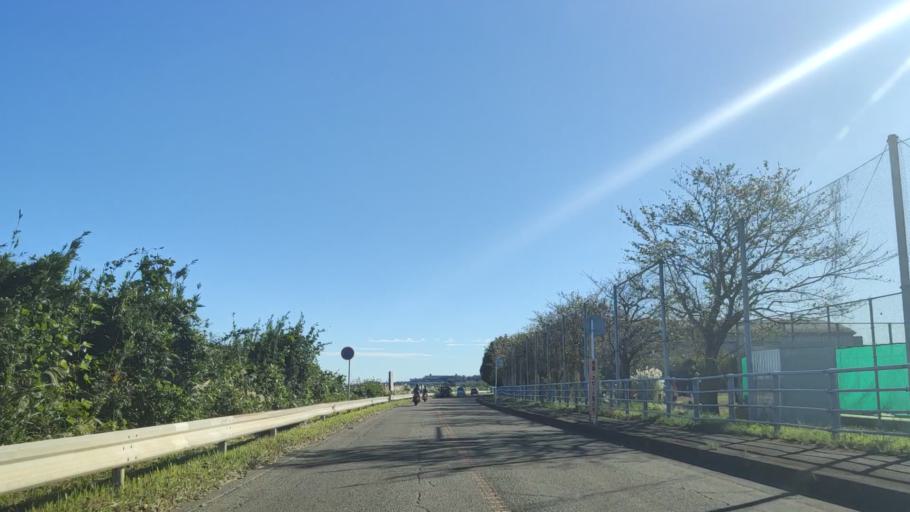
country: JP
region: Kanagawa
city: Zama
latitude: 35.5077
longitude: 139.3740
